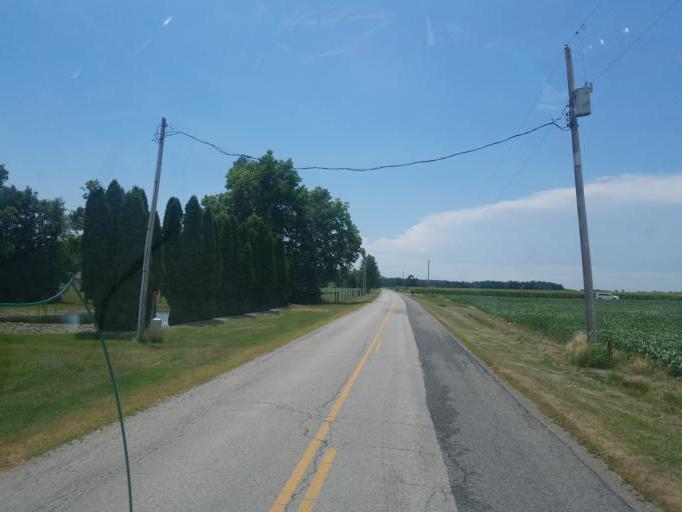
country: US
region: Ohio
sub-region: Paulding County
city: Antwerp
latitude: 41.1884
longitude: -84.7739
